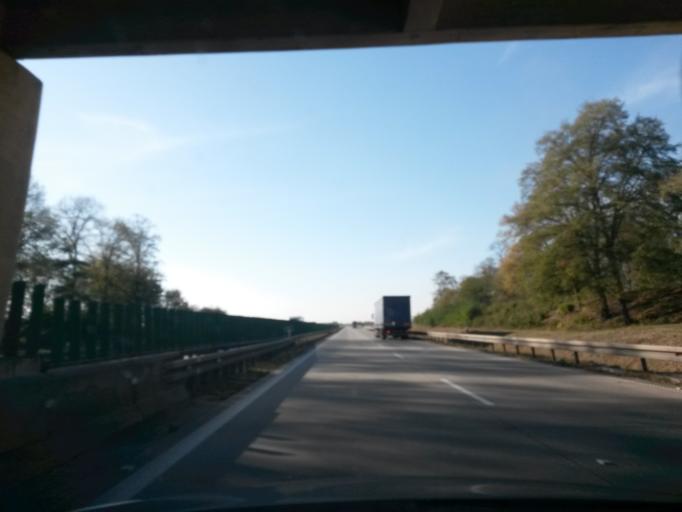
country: PL
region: Lower Silesian Voivodeship
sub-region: Powiat sredzki
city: Ciechow
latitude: 51.0515
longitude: 16.5557
